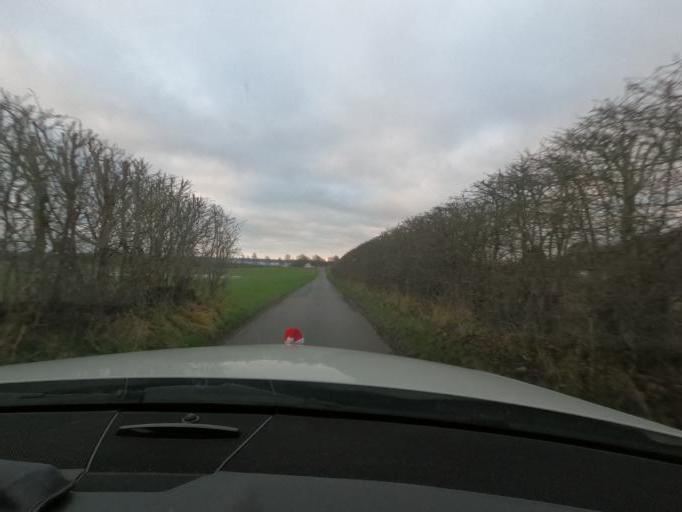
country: DK
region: South Denmark
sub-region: Sonderborg Kommune
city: Sonderborg
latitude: 54.9015
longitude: 9.8515
